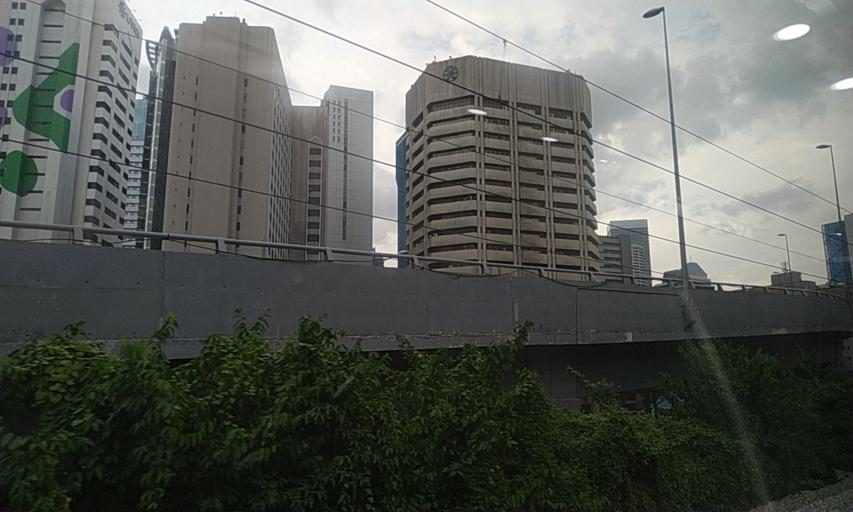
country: MY
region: Kuala Lumpur
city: Kuala Lumpur
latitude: 3.1589
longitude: 101.6930
